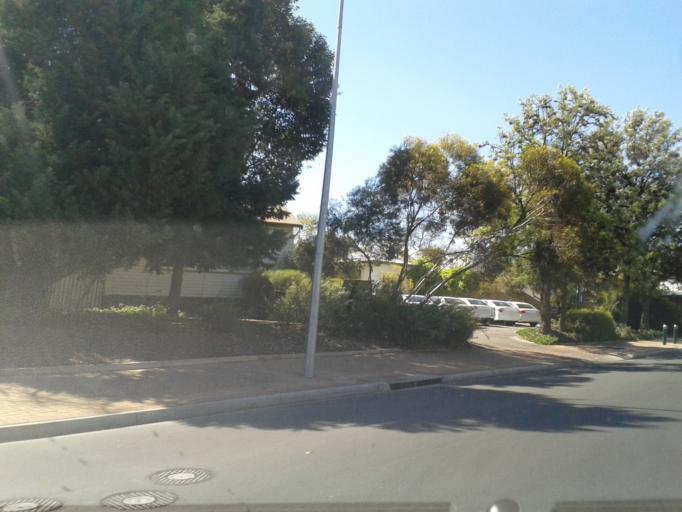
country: AU
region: South Australia
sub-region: Berri and Barmera
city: Berri
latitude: -34.2849
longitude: 140.6027
